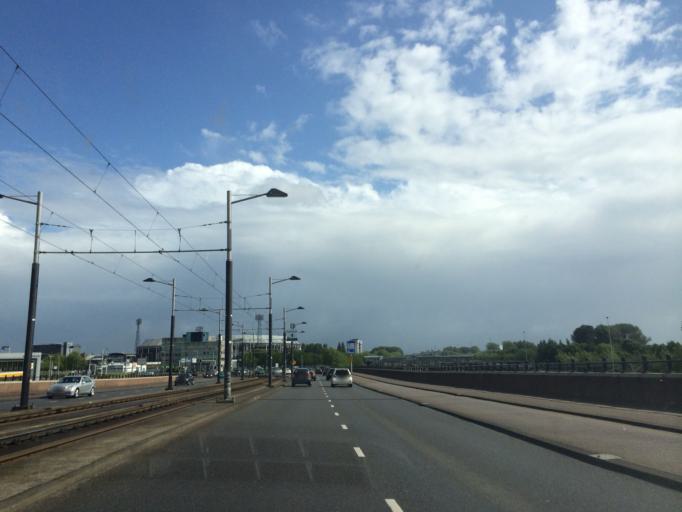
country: NL
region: South Holland
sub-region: Gemeente Rotterdam
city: Rotterdam
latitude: 51.8984
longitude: 4.5157
